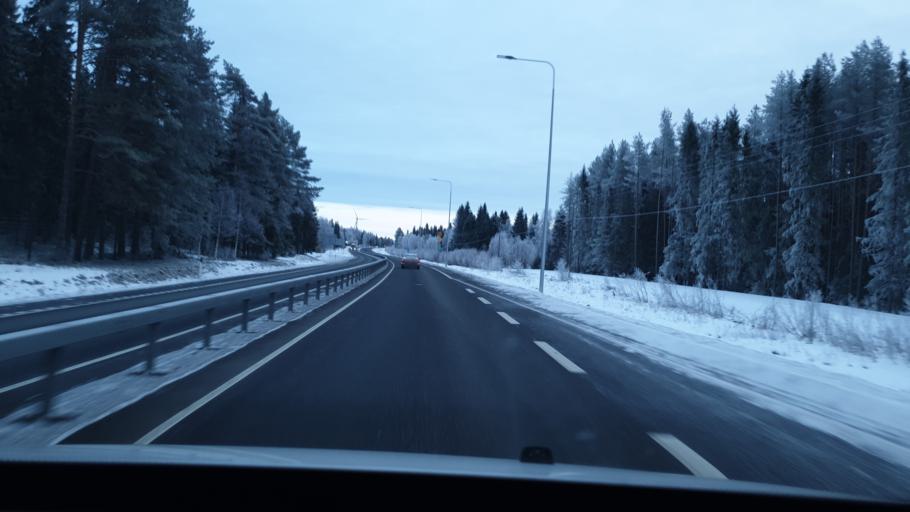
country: FI
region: Lapland
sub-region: Kemi-Tornio
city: Simo
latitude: 65.6685
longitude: 24.9408
